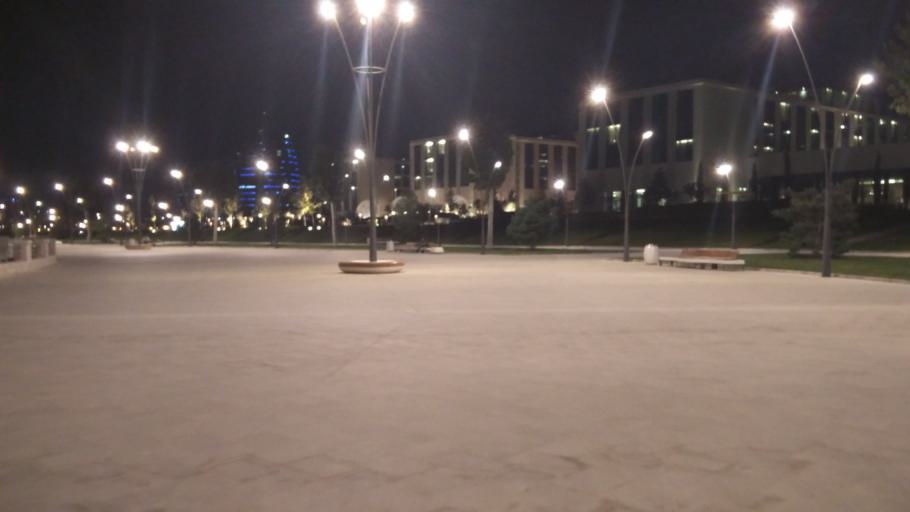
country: AZ
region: Baki
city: Baku
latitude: 40.3740
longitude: 49.8848
